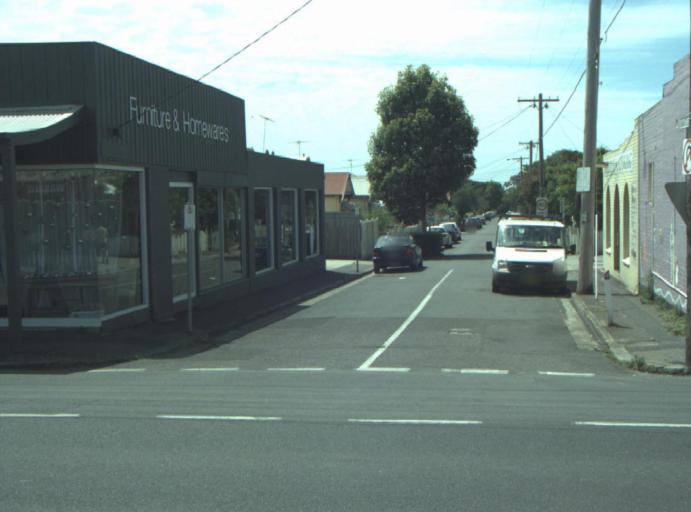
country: AU
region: Victoria
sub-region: Greater Geelong
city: Geelong West
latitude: -38.1373
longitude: 144.3489
